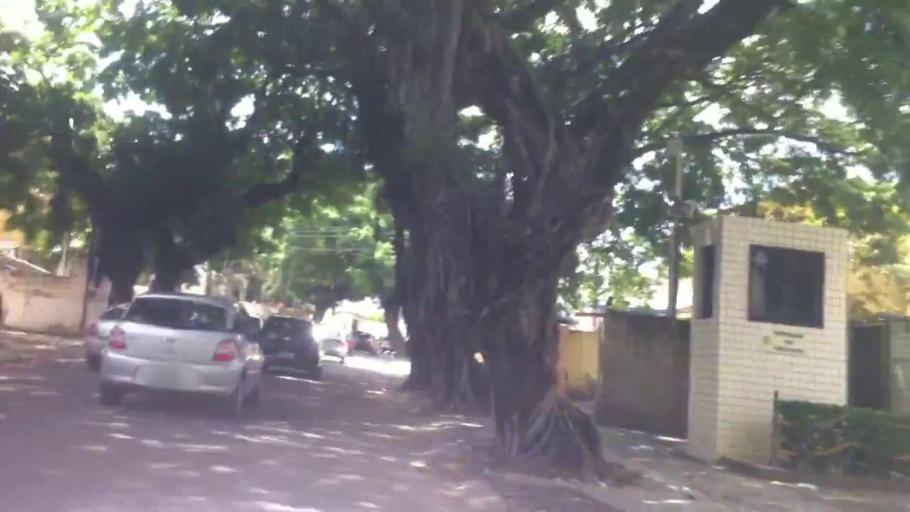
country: BR
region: Pernambuco
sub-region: Recife
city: Recife
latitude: -8.0526
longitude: -34.8924
